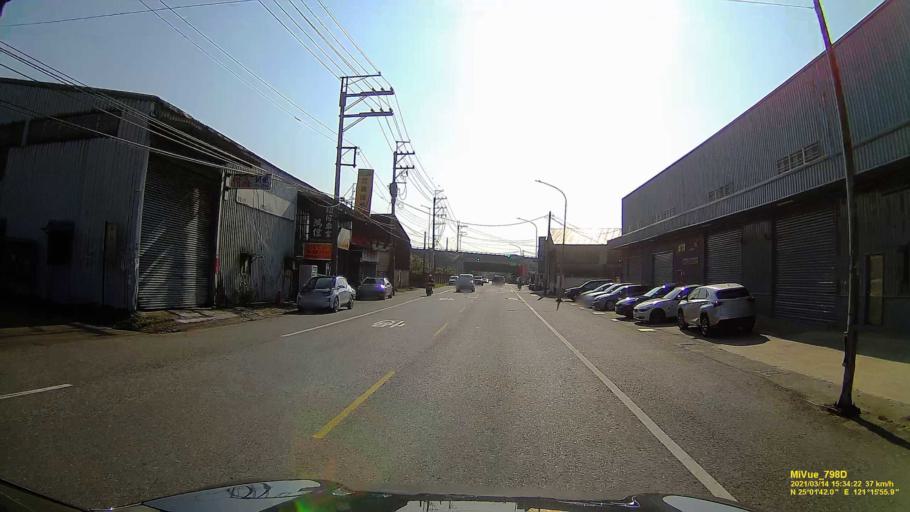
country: TW
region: Taiwan
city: Taoyuan City
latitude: 25.0282
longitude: 121.2653
